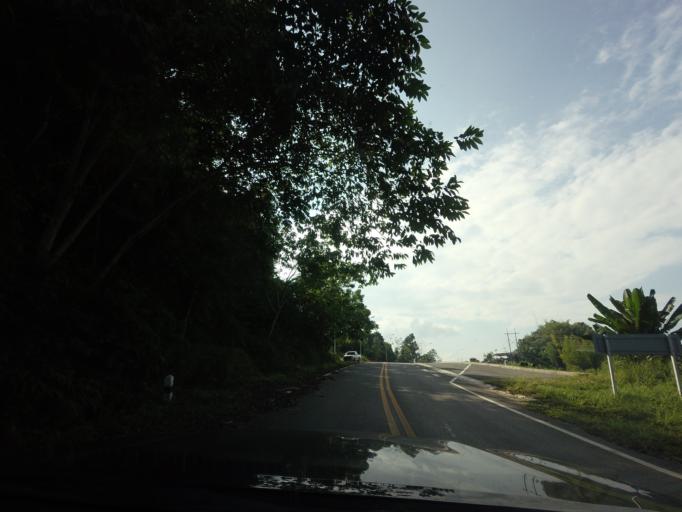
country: TH
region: Nan
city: Na Noi
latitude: 18.3692
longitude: 100.8308
